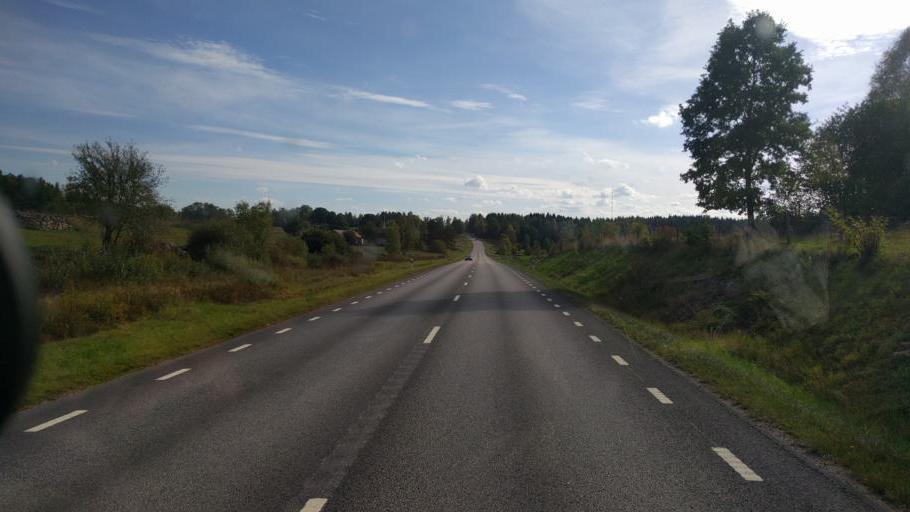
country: SE
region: OEstergoetland
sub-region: Kinda Kommun
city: Kisa
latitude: 57.9269
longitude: 15.6736
